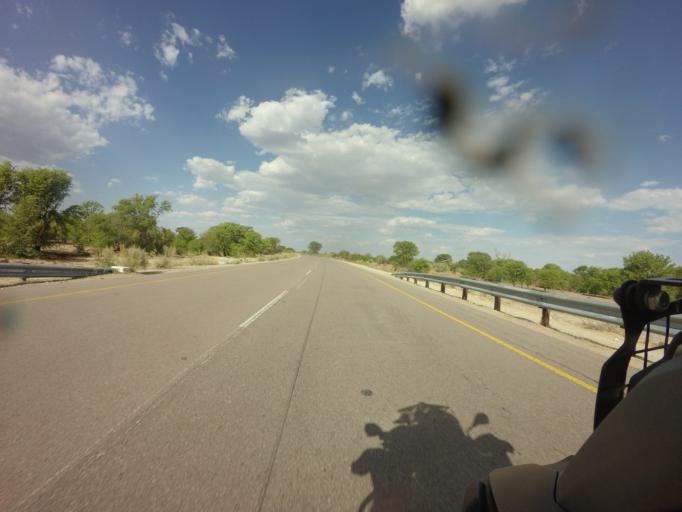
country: AO
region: Cunene
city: Ondjiva
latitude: -16.7264
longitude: 15.2446
